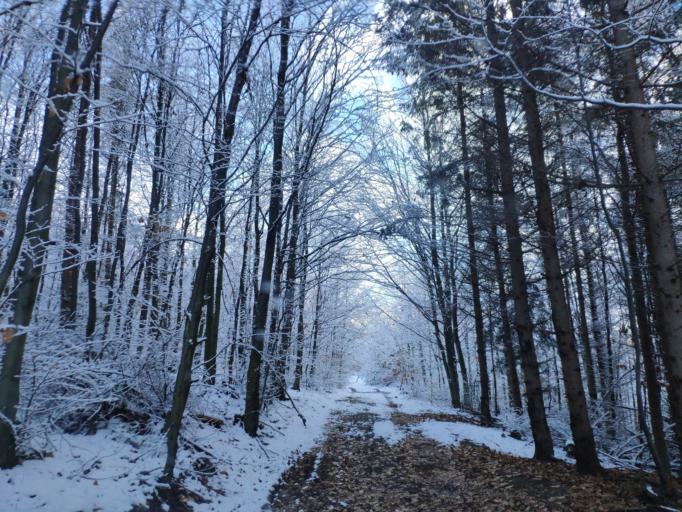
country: SK
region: Kosicky
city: Moldava nad Bodvou
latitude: 48.7422
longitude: 21.0939
